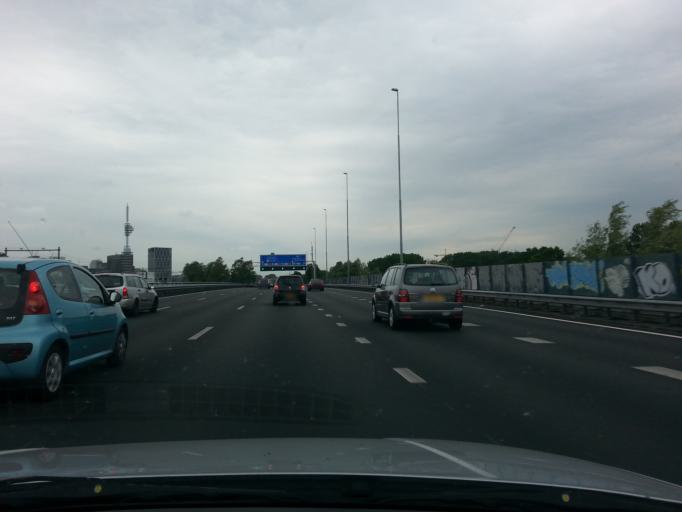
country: NL
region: North Holland
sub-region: Gemeente Ouder-Amstel
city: Ouderkerk aan de Amstel
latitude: 52.3326
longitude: 4.8999
